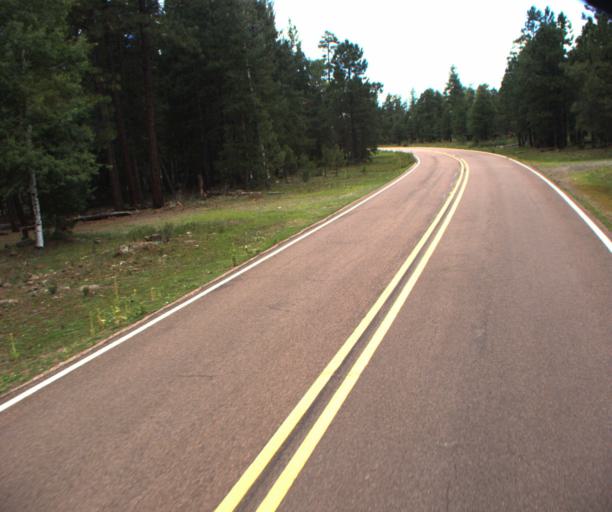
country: US
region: Arizona
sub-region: Navajo County
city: Pinetop-Lakeside
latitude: 34.0058
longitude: -109.7655
